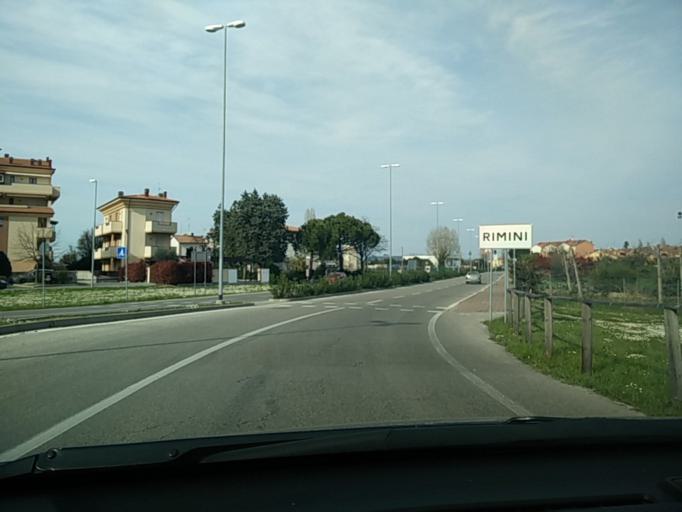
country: IT
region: Emilia-Romagna
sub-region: Provincia di Rimini
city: Santa Giustina
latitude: 44.0727
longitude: 12.5155
